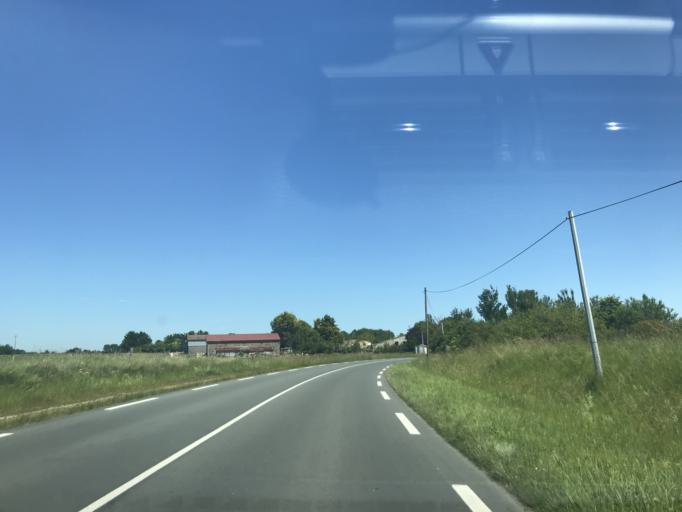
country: FR
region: Poitou-Charentes
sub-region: Departement de la Charente-Maritime
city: Meschers-sur-Gironde
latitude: 45.5621
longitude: -0.9399
